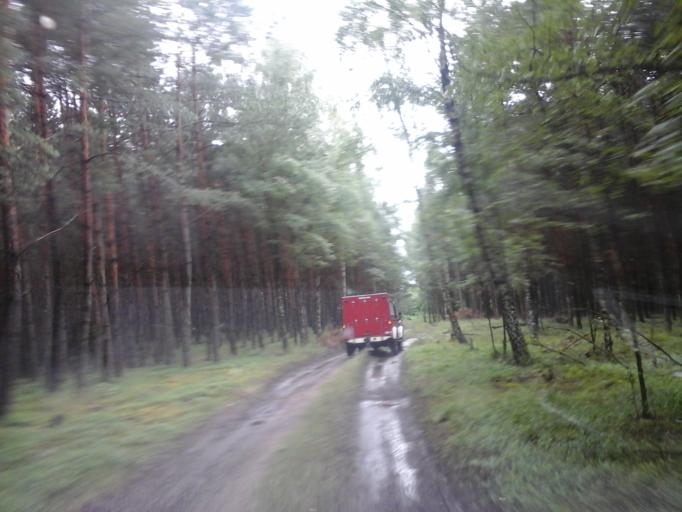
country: PL
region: West Pomeranian Voivodeship
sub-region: Powiat choszczenski
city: Bierzwnik
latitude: 52.9856
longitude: 15.5975
